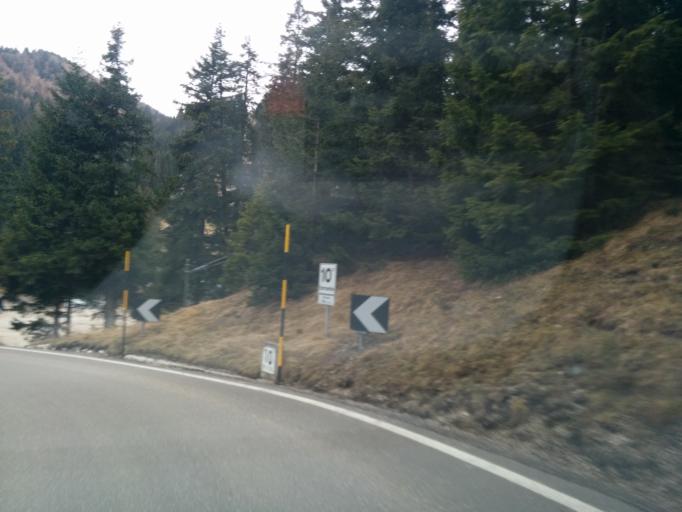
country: IT
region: Trentino-Alto Adige
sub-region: Provincia di Trento
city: Canazei
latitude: 46.4919
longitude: 11.7826
